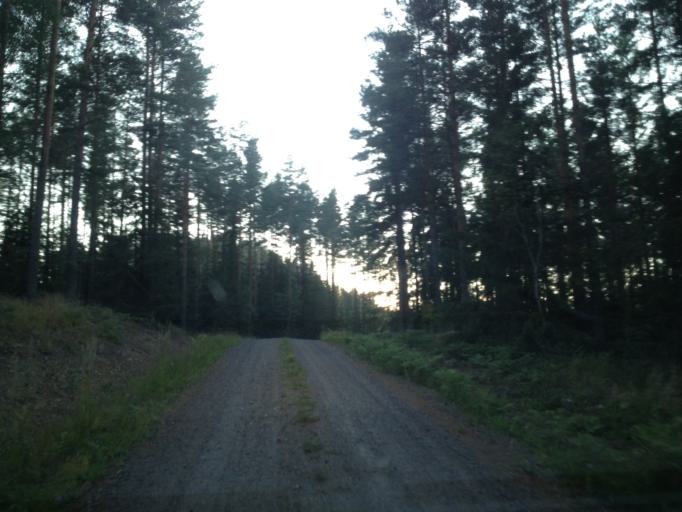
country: SE
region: Kalmar
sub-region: Vasterviks Kommun
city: Overum
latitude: 58.0227
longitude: 16.1170
